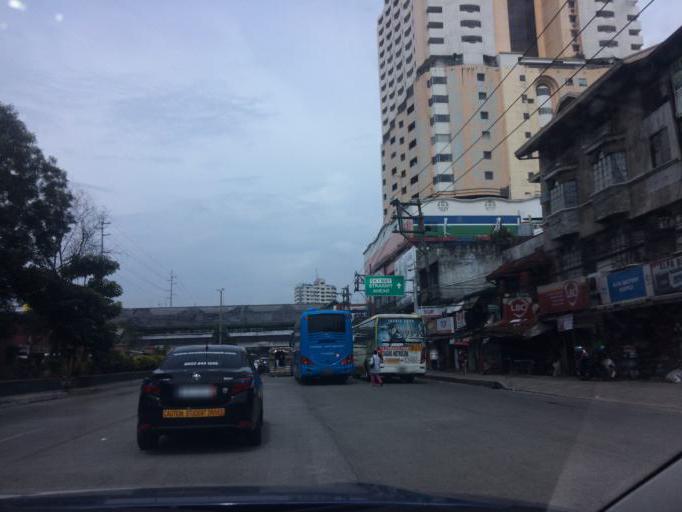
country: PH
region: Metro Manila
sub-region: Makati City
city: Makati City
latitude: 14.5536
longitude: 120.9957
